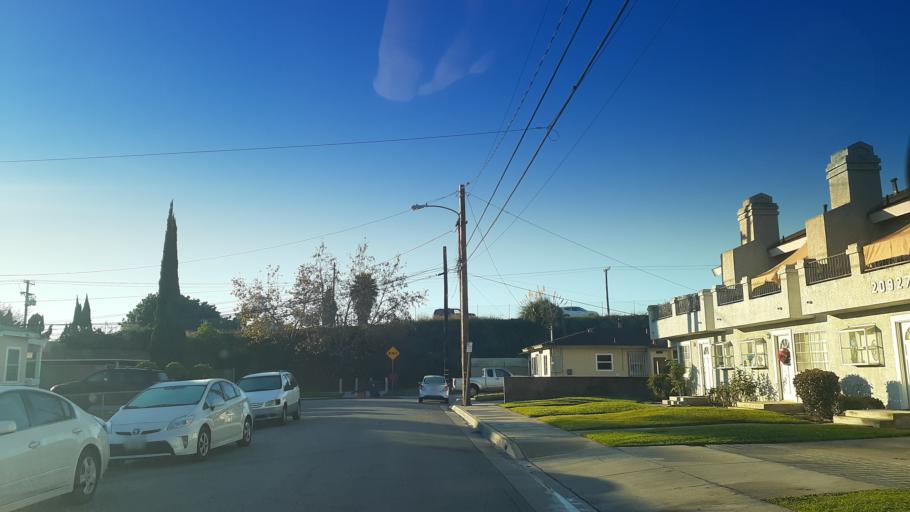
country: US
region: California
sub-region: Los Angeles County
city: Hawaiian Gardens
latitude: 33.8394
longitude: -118.0868
